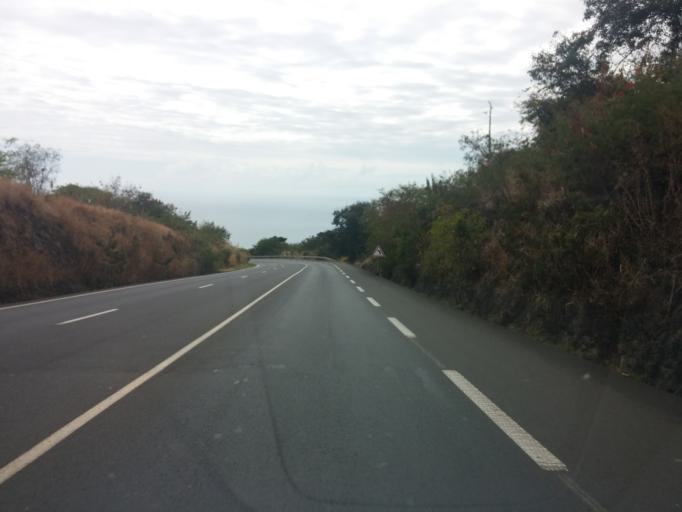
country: RE
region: Reunion
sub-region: Reunion
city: Saint-Paul
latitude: -21.0232
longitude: 55.2738
